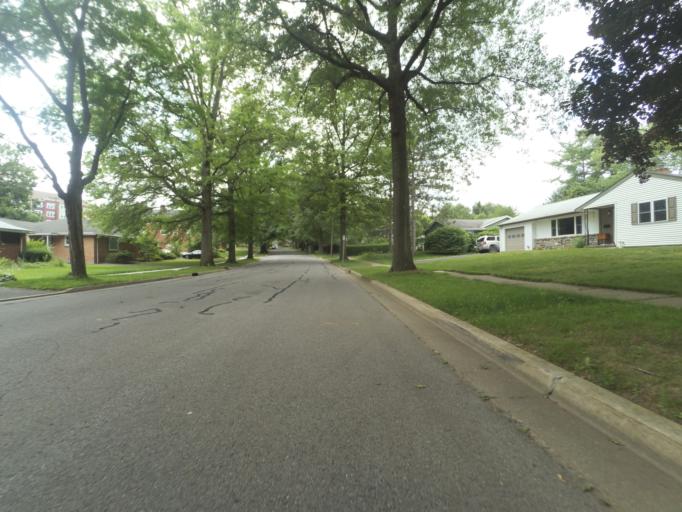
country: US
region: Pennsylvania
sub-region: Centre County
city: State College
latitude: 40.7861
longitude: -77.8433
